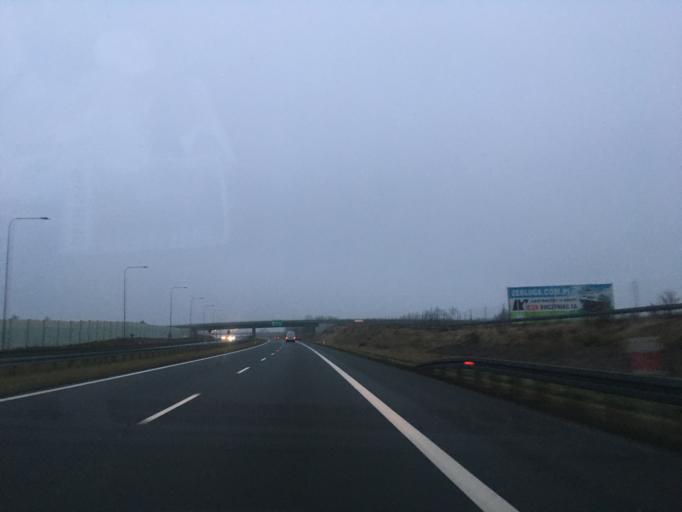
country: PL
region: Warmian-Masurian Voivodeship
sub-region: Powiat ostrodzki
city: Maldyty
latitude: 53.9613
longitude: 19.6979
